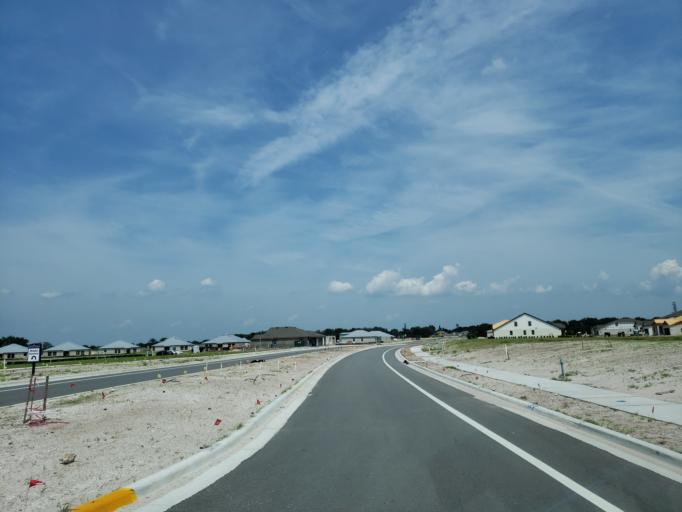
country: US
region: Florida
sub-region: Hillsborough County
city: Riverview
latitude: 27.8405
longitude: -82.3385
